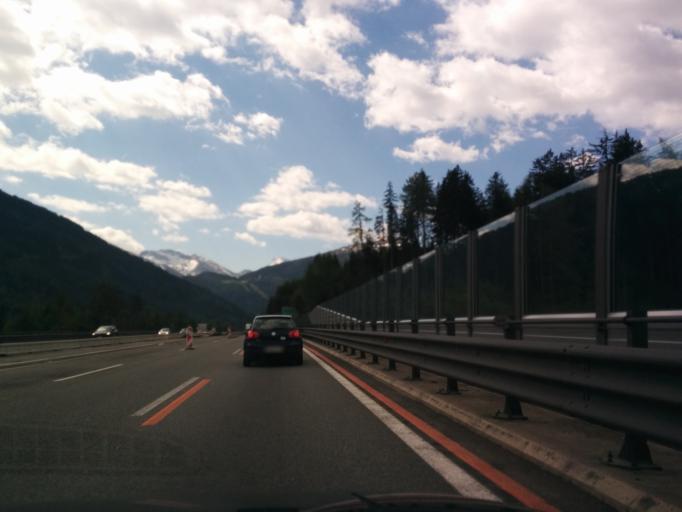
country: AT
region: Tyrol
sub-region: Politischer Bezirk Innsbruck Land
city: Gries am Brenner
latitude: 47.0566
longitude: 11.4801
